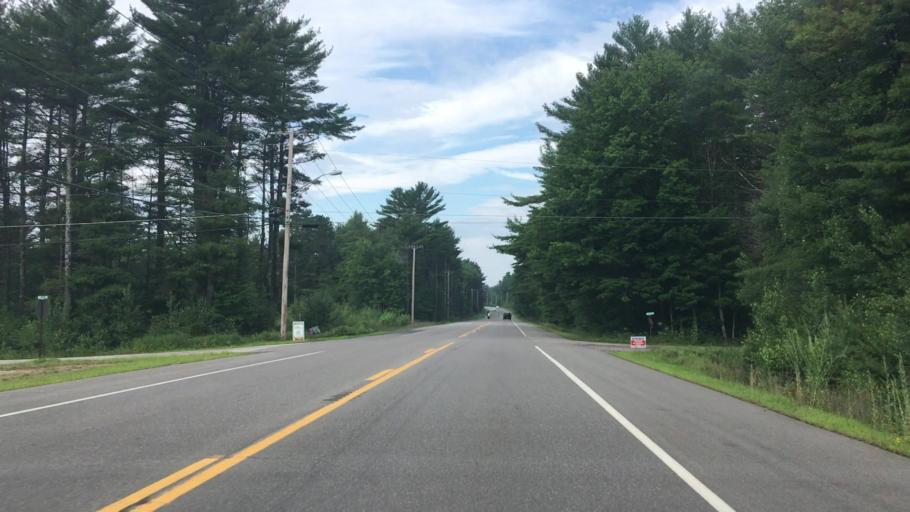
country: US
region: Maine
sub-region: York County
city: Lebanon
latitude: 43.3667
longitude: -70.9009
